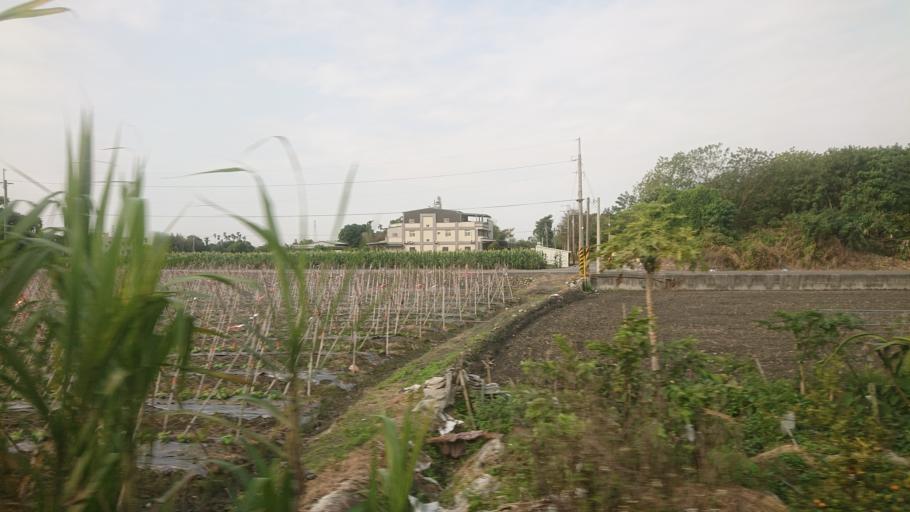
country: TW
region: Taiwan
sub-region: Nantou
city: Nantou
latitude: 23.8935
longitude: 120.5809
